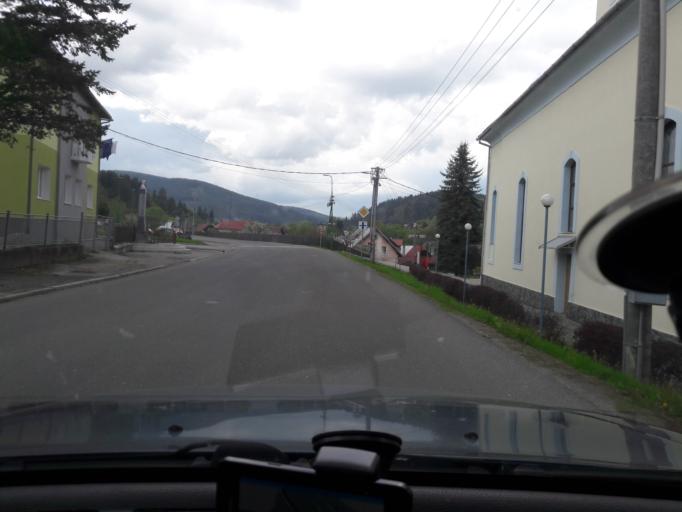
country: SK
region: Banskobystricky
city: Cierny Balog
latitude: 48.7462
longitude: 19.6555
